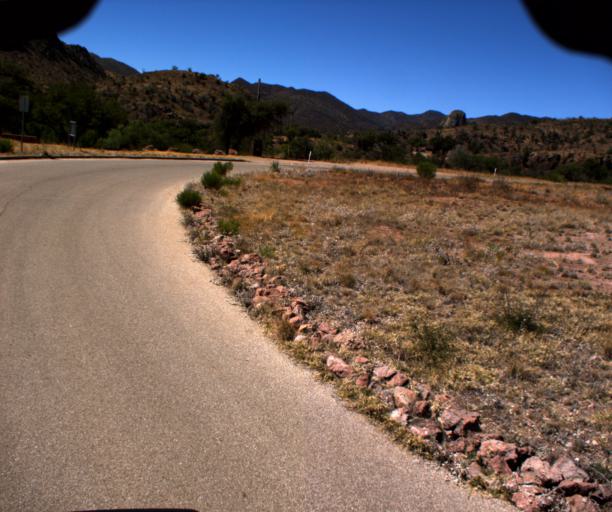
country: US
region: Arizona
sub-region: Santa Cruz County
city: Rio Rico
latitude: 31.4021
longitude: -111.0879
